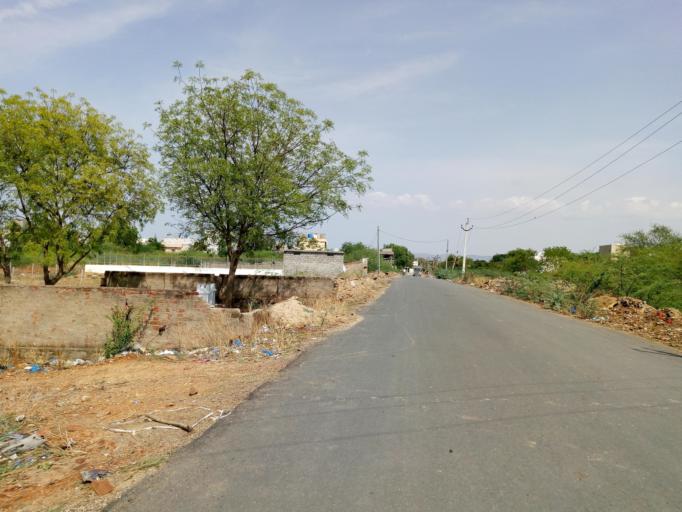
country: IN
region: Andhra Pradesh
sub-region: Prakasam
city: Cumbum
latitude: 15.5850
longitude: 79.1087
